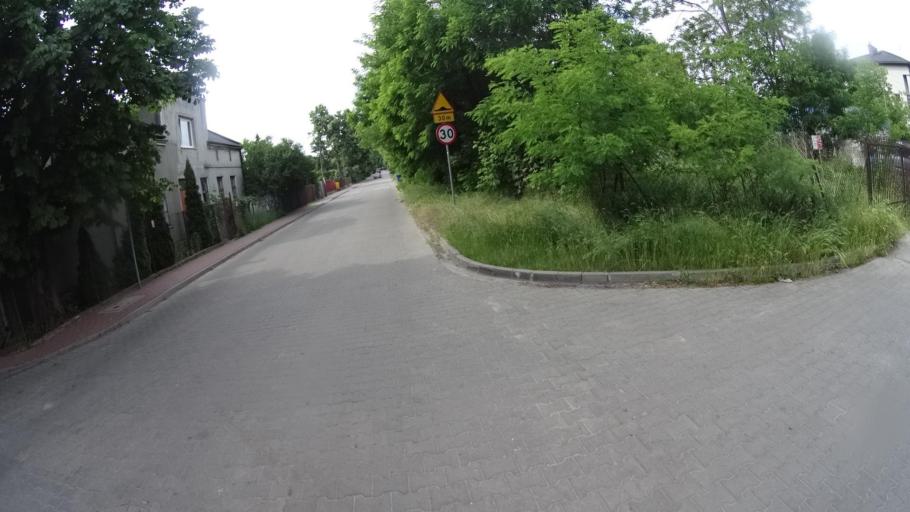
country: PL
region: Masovian Voivodeship
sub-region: Powiat pruszkowski
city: Piastow
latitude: 52.1932
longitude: 20.8523
